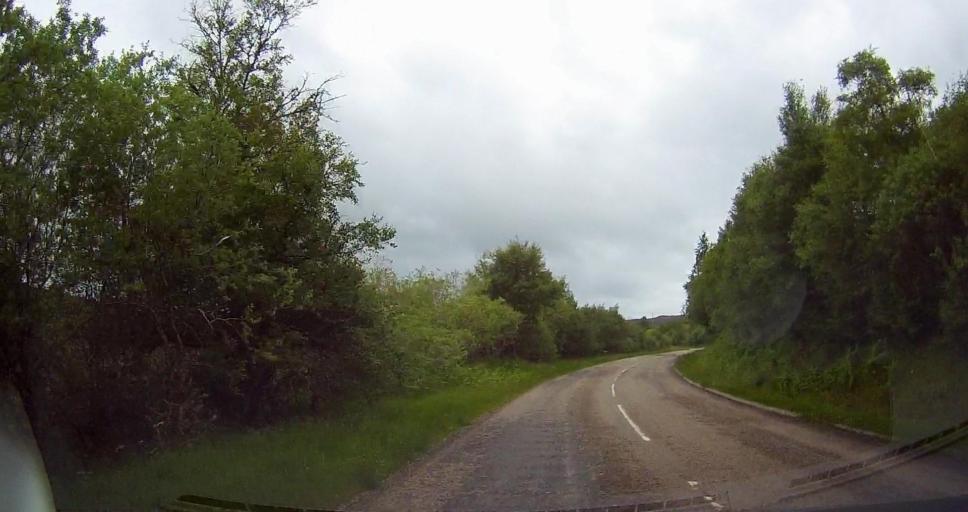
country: GB
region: Scotland
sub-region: Highland
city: Dornoch
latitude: 58.0172
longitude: -4.3245
